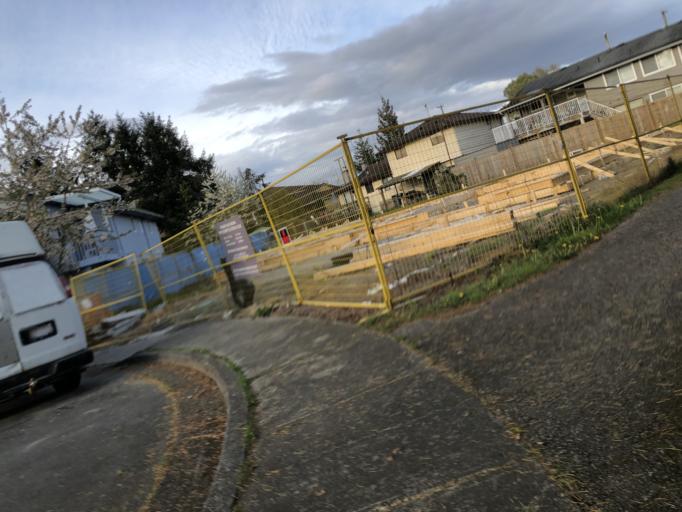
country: CA
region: British Columbia
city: Richmond
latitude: 49.1471
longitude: -123.1152
